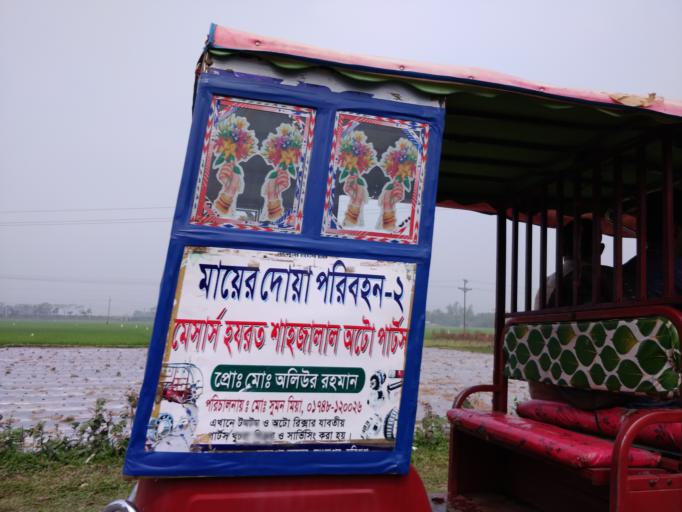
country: BD
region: Sylhet
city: Habiganj
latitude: 24.1651
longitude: 91.3538
